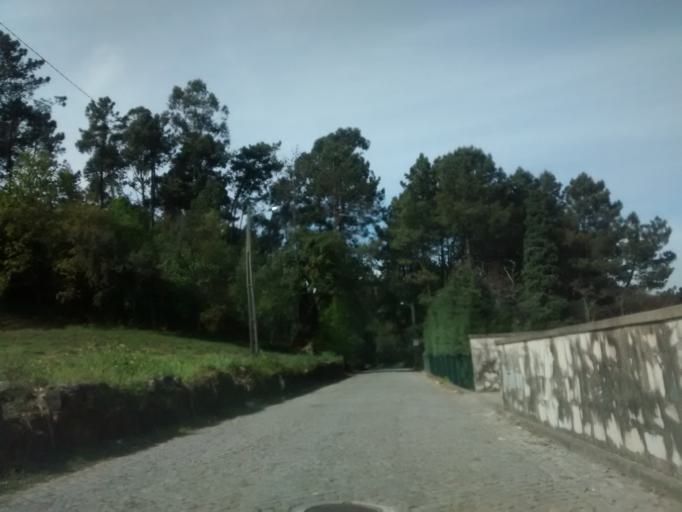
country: PT
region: Braga
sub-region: Braga
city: Braga
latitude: 41.5445
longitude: -8.4431
